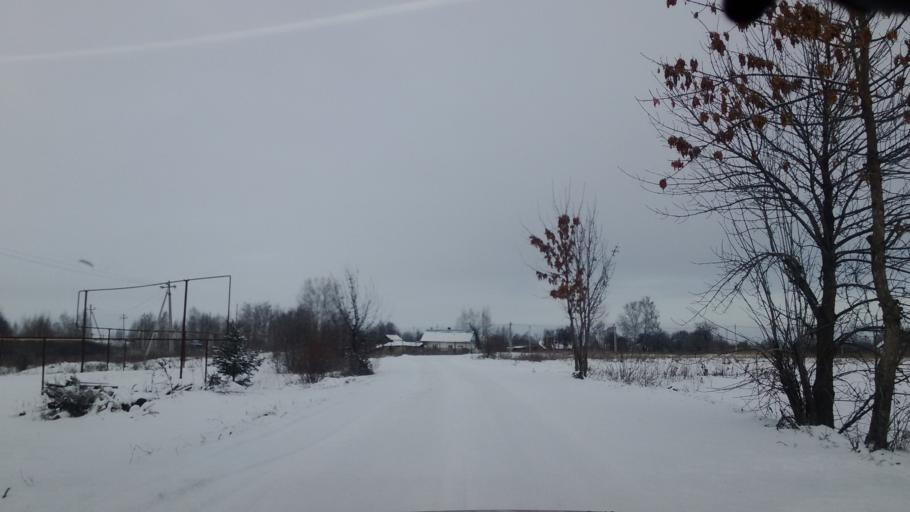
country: RU
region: Tula
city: Bogoroditsk
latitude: 53.7508
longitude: 38.1065
